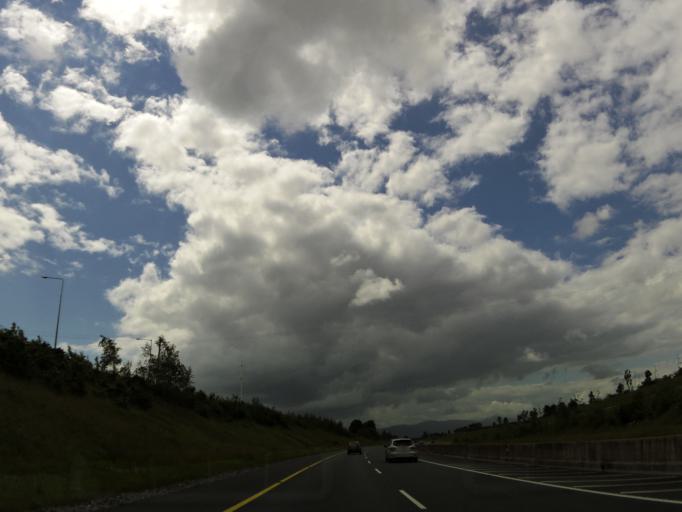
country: IE
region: Munster
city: Cashel
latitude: 52.4976
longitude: -7.8886
